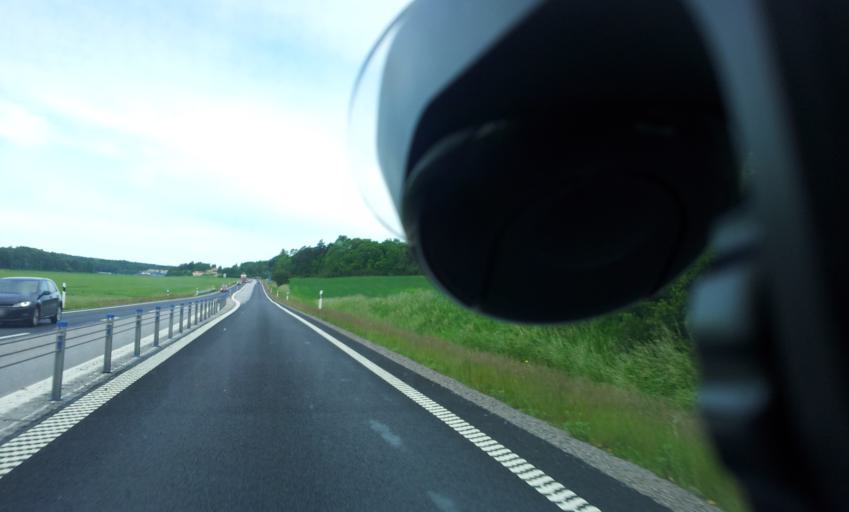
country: SE
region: OEstergoetland
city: Lindo
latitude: 58.5465
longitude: 16.2629
